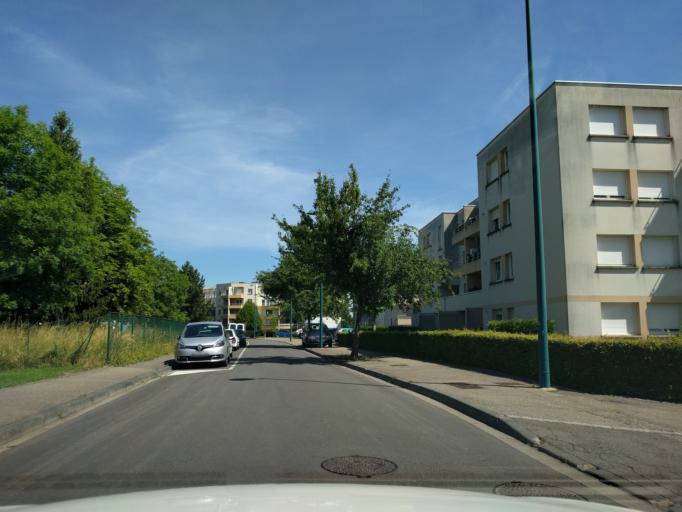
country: FR
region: Lorraine
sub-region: Departement de la Moselle
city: Saint-Julien-les-Metz
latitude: 49.1042
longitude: 6.2050
